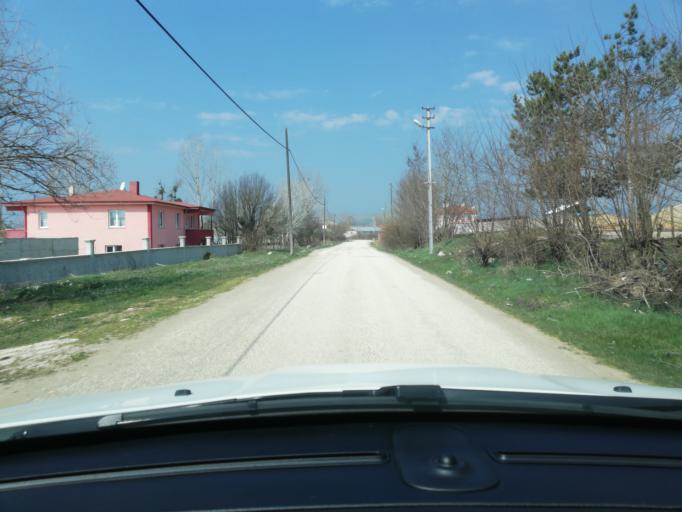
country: TR
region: Kastamonu
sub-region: Cide
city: Kastamonu
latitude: 41.4580
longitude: 33.7655
